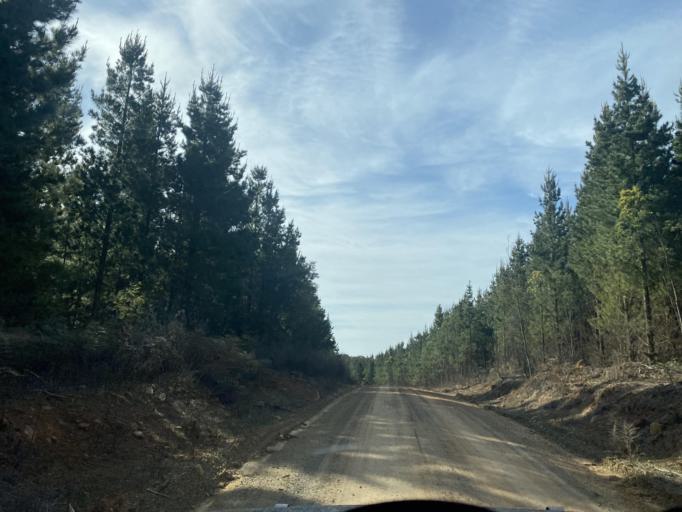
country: AU
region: Victoria
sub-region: Mansfield
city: Mansfield
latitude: -36.8750
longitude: 146.1838
